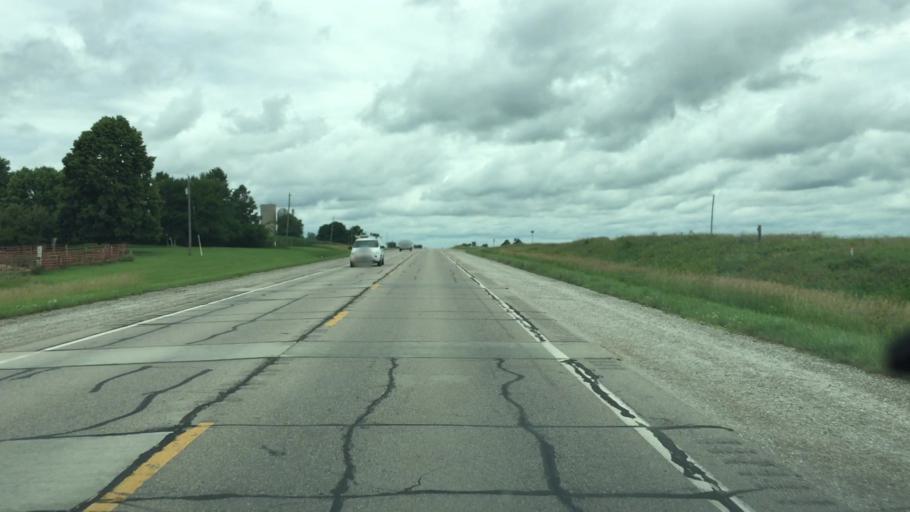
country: US
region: Iowa
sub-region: Jasper County
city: Monroe
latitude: 41.5503
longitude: -93.0970
